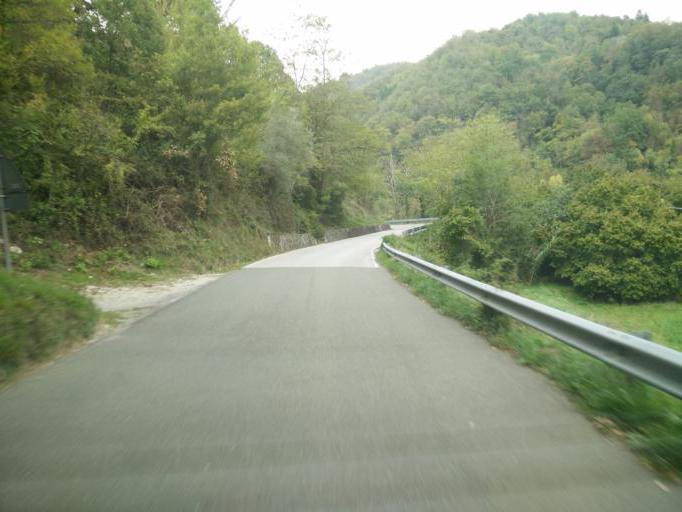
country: IT
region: Tuscany
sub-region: Provincia di Massa-Carrara
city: Casola in Lunigiana
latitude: 44.1940
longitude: 10.1533
